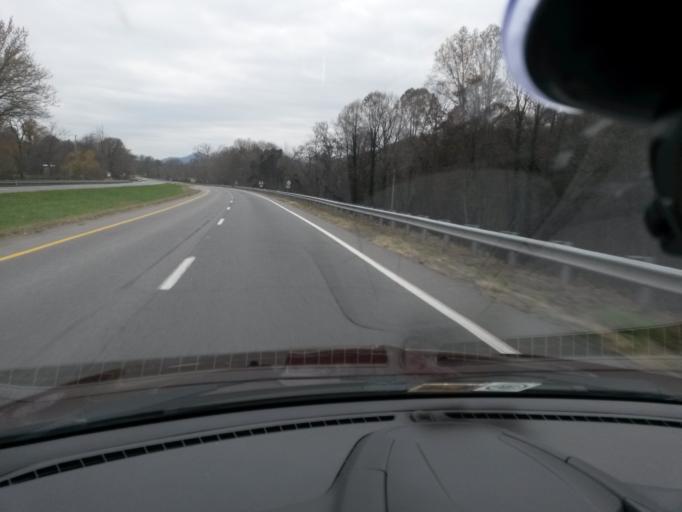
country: US
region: Virginia
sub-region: Nelson County
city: Nellysford
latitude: 37.8858
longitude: -78.7113
